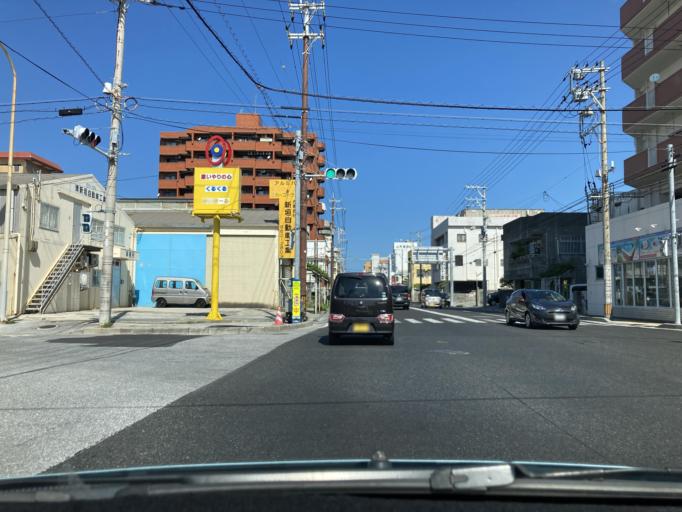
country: JP
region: Okinawa
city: Naha-shi
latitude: 26.2367
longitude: 127.6816
